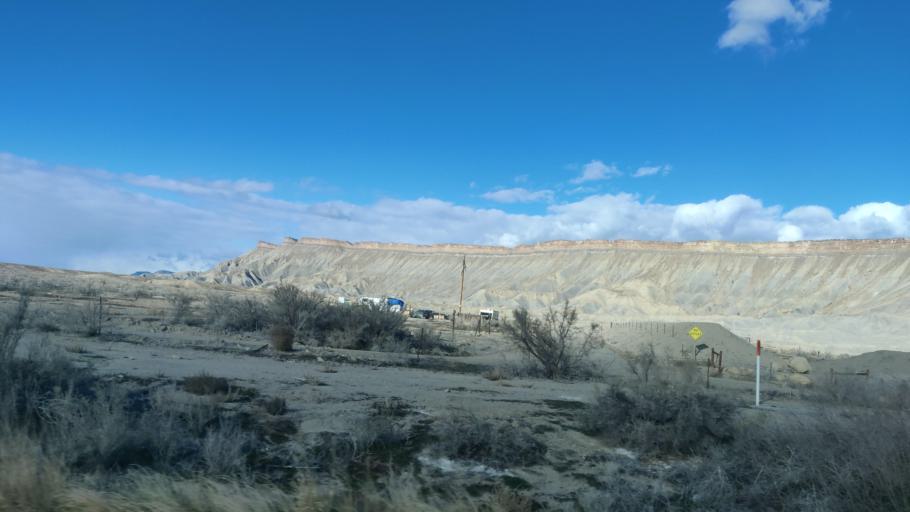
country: US
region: Colorado
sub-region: Mesa County
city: Clifton
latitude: 39.1089
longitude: -108.4270
